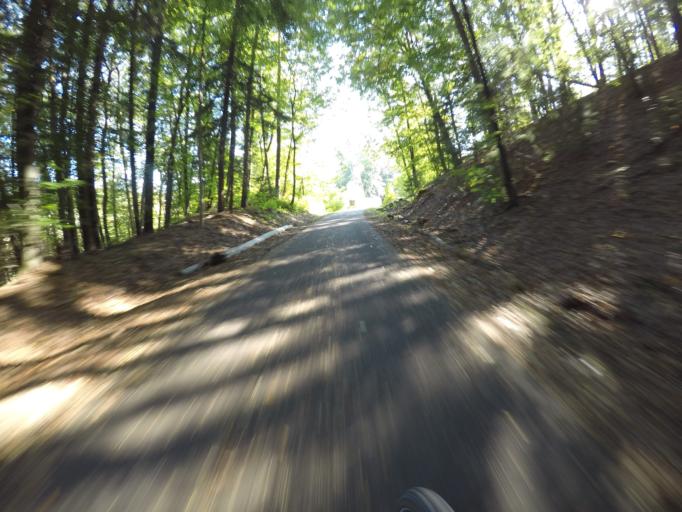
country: DE
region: Baden-Wuerttemberg
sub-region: Regierungsbezirk Stuttgart
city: Steinenbronn
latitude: 48.6780
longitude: 9.1259
